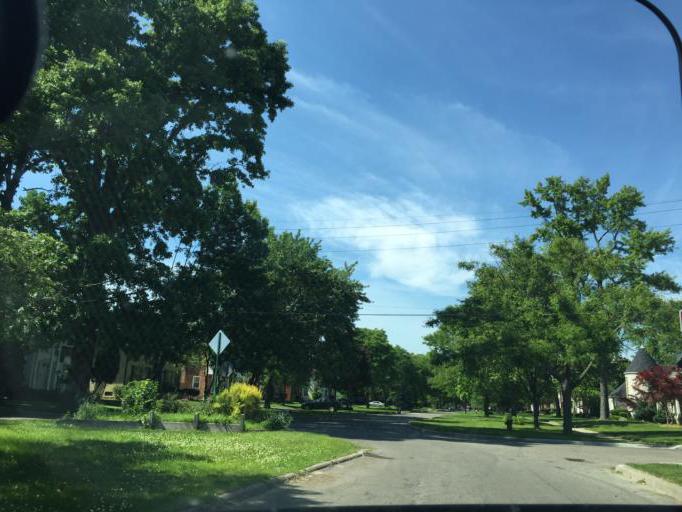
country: US
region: Michigan
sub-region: Oakland County
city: Southfield
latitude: 42.4115
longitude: -83.2289
